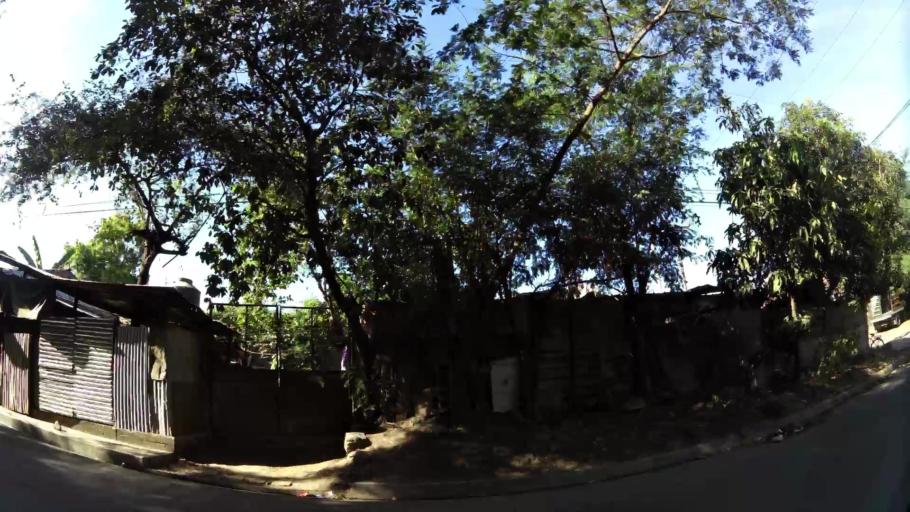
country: SV
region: San Miguel
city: San Miguel
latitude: 13.4779
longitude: -88.1919
